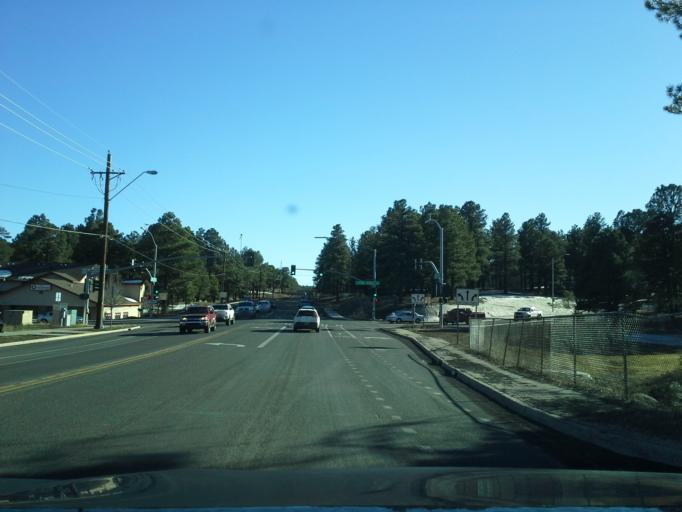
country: US
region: Arizona
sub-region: Coconino County
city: Flagstaff
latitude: 35.1804
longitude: -111.6483
